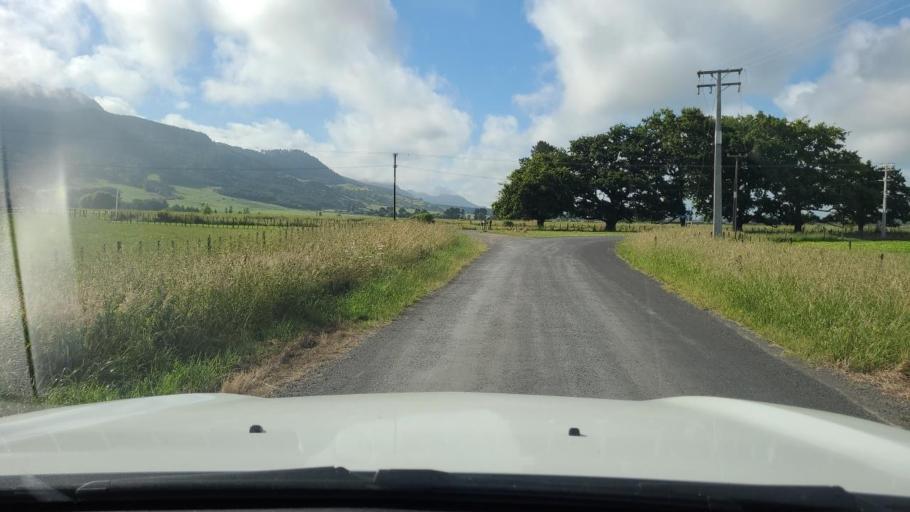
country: NZ
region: Bay of Plenty
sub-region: Western Bay of Plenty District
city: Katikati
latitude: -37.6151
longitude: 175.7959
